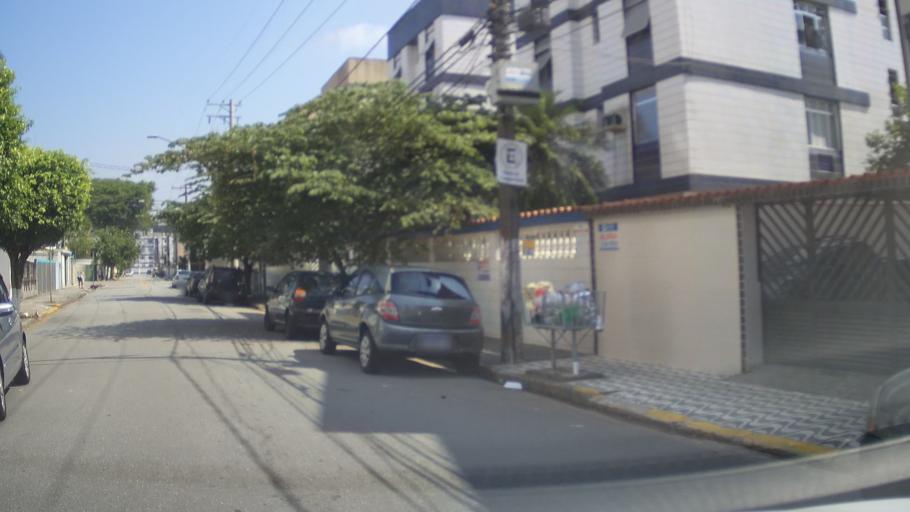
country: BR
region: Sao Paulo
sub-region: Santos
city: Santos
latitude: -23.9765
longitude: -46.3026
